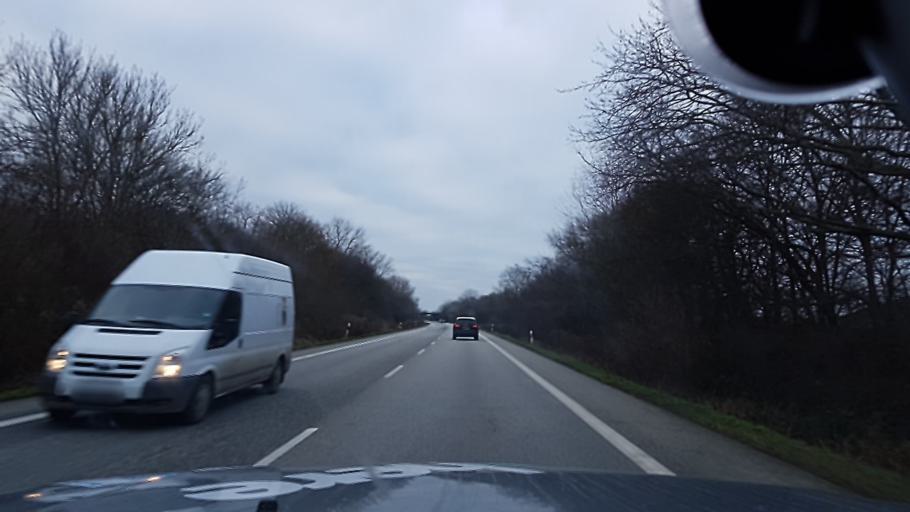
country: DE
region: Schleswig-Holstein
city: Fehmarn
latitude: 54.4303
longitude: 11.1395
